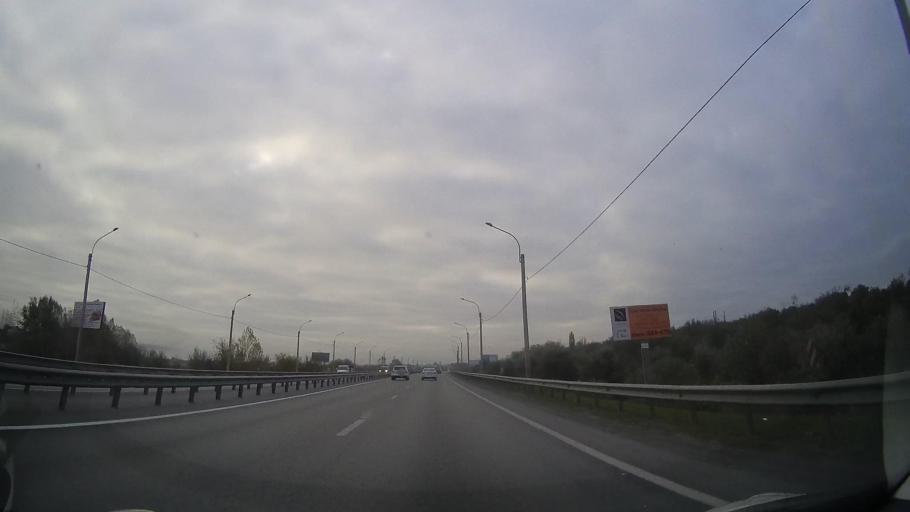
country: RU
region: Rostov
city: Bataysk
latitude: 47.1468
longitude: 39.7744
